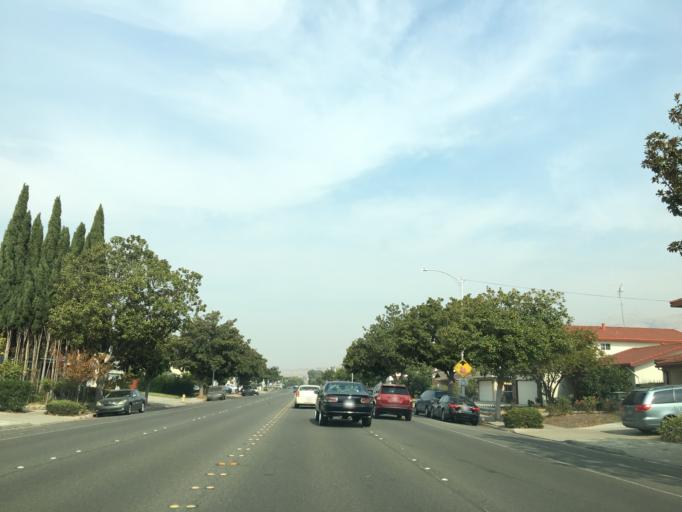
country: US
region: California
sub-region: Santa Clara County
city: Milpitas
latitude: 37.4319
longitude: -121.8830
